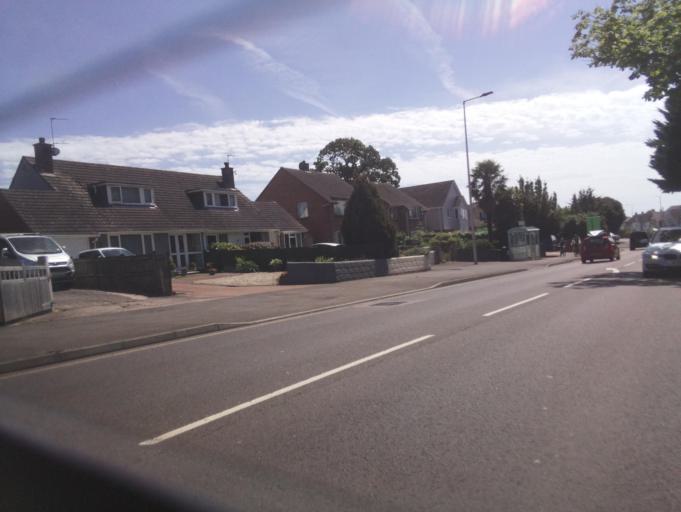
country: GB
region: England
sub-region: Devon
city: Exmouth
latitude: 50.6328
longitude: -3.4103
